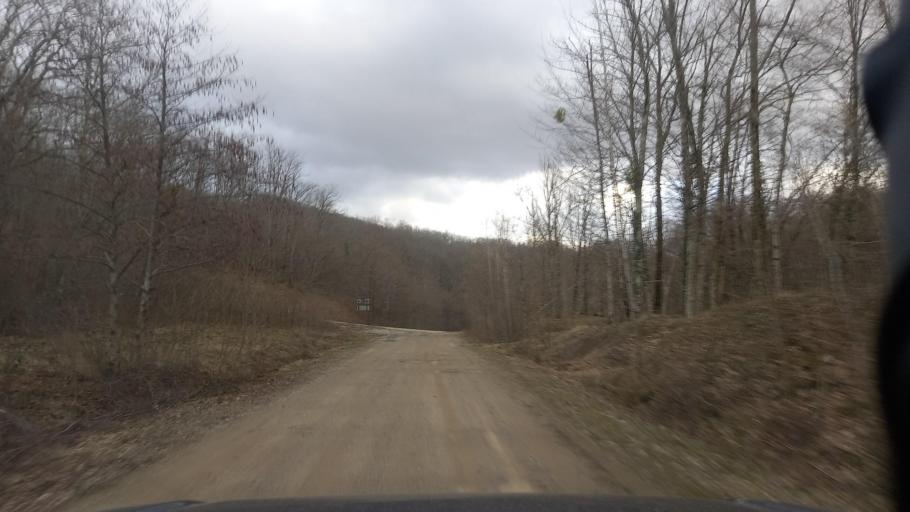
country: RU
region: Krasnodarskiy
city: Dzhubga
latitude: 44.4845
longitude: 38.7858
